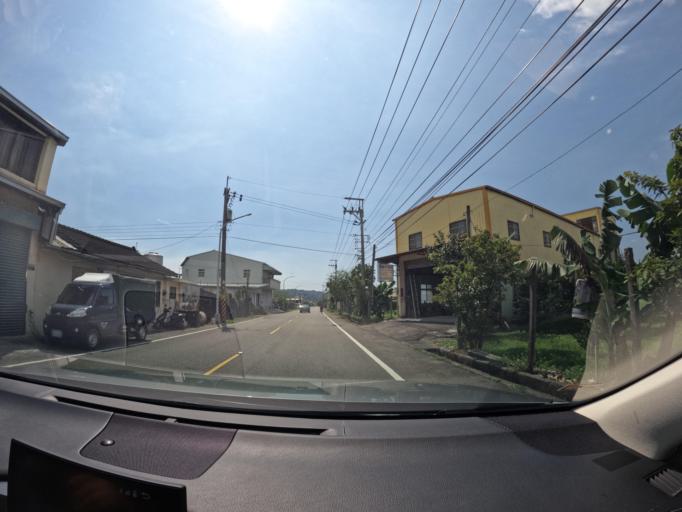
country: TW
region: Taiwan
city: Fengyuan
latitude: 24.3050
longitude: 120.8103
